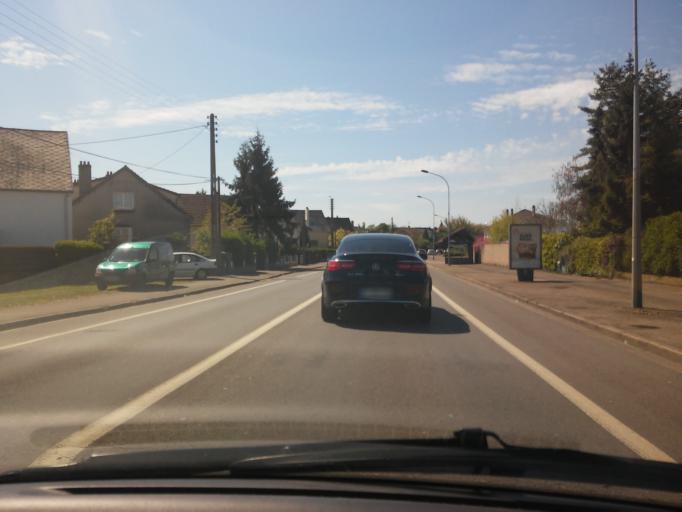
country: FR
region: Lorraine
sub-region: Departement de la Moselle
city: Hagondange
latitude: 49.2583
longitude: 6.1589
